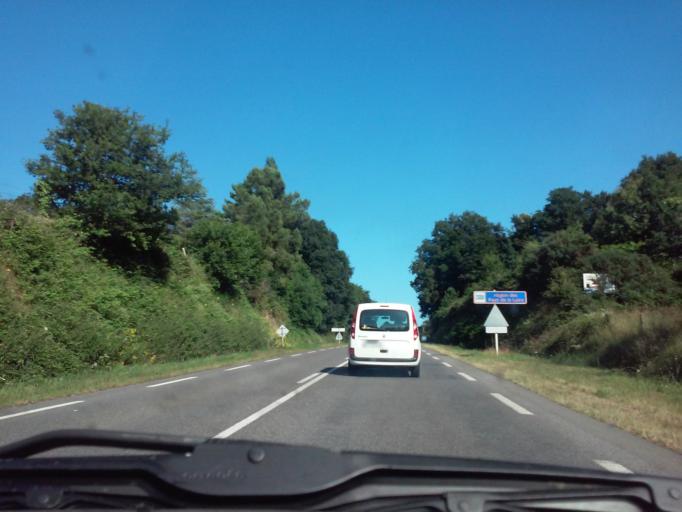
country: FR
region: Brittany
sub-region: Departement d'Ille-et-Vilaine
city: La Chapelle-Janson
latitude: 48.3145
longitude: -1.0601
